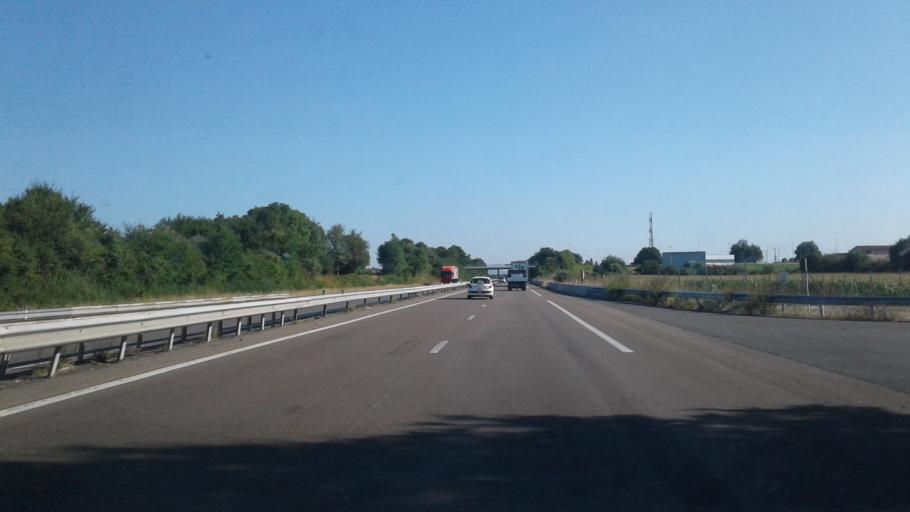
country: FR
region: Rhone-Alpes
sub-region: Departement de l'Ain
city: Chateau-Gaillard
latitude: 45.9724
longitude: 5.3092
